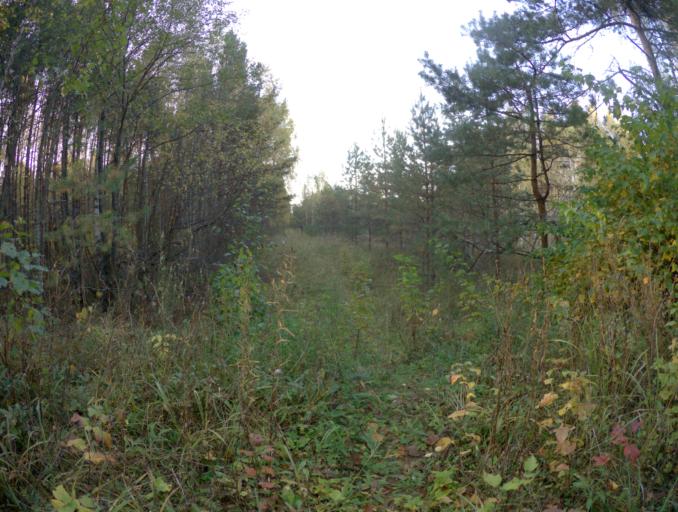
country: RU
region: Vladimir
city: Raduzhnyy
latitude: 56.0235
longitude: 40.2766
